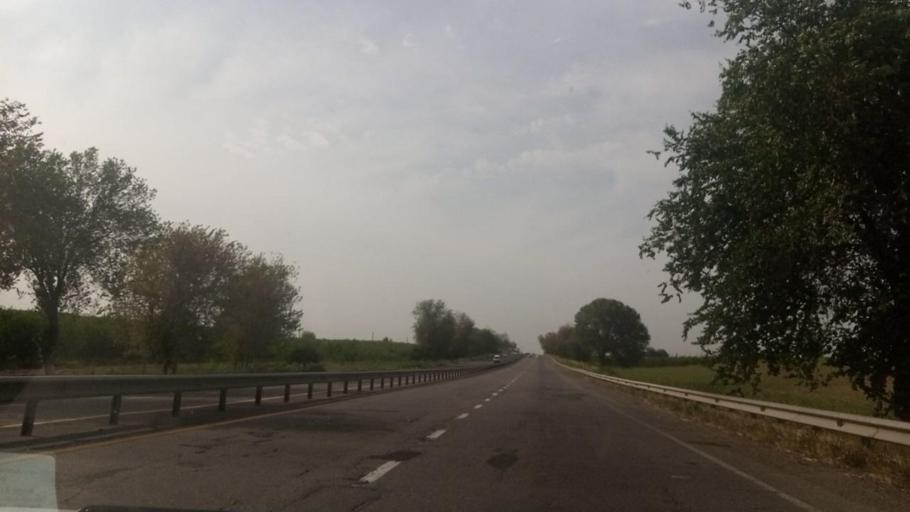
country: UZ
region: Toshkent
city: Tuytepa
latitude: 41.0938
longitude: 69.4607
